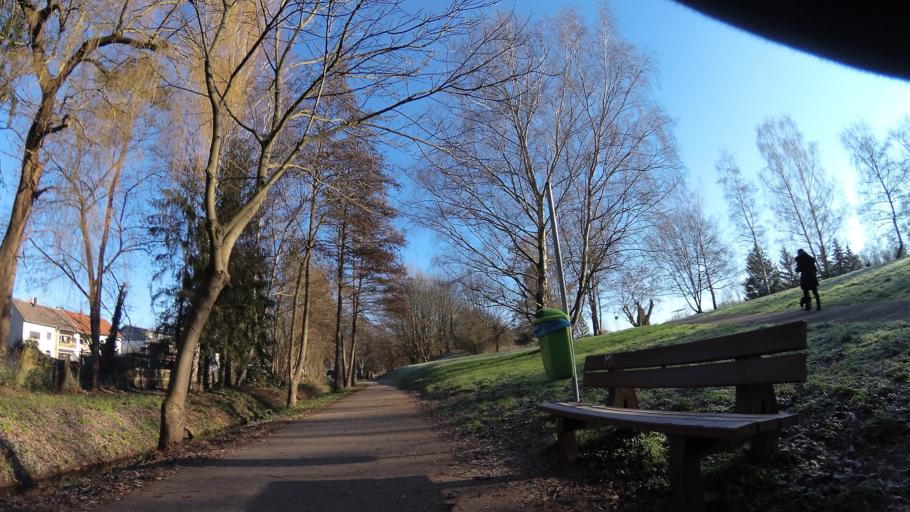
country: DE
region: Saarland
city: Ensdorf
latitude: 49.3297
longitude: 6.7806
